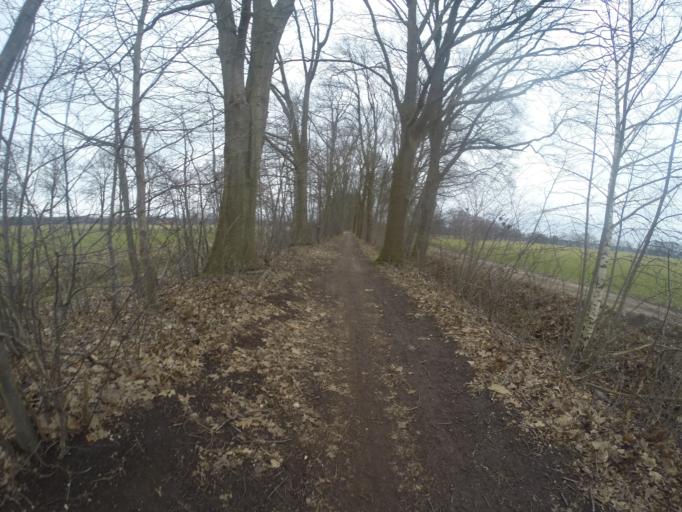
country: NL
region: Gelderland
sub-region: Gemeente Bronckhorst
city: Zelhem
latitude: 52.0174
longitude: 6.3664
